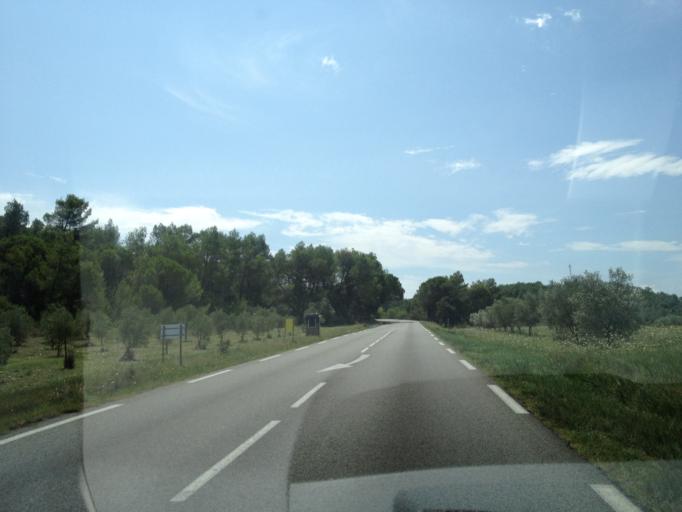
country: FR
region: Languedoc-Roussillon
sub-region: Departement du Gard
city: Villevieille
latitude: 43.8763
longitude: 4.0951
